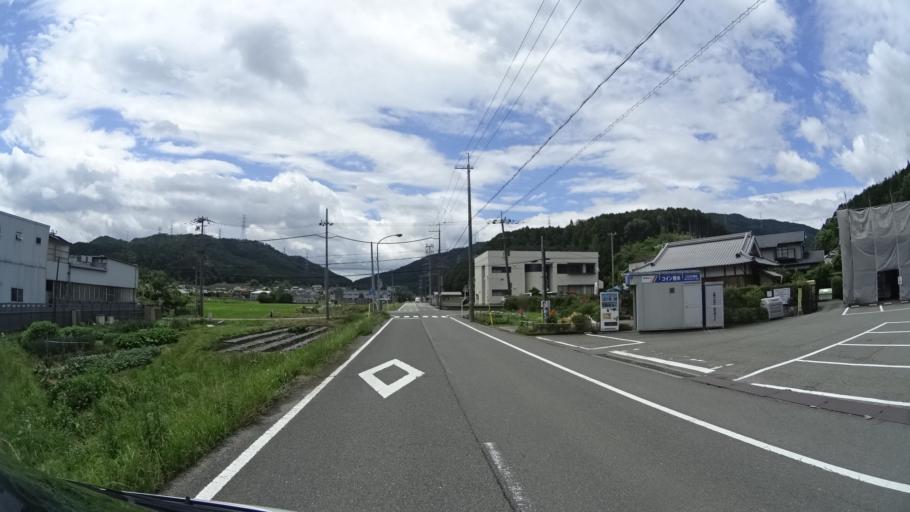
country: JP
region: Kyoto
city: Kameoka
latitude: 35.0101
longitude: 135.4819
